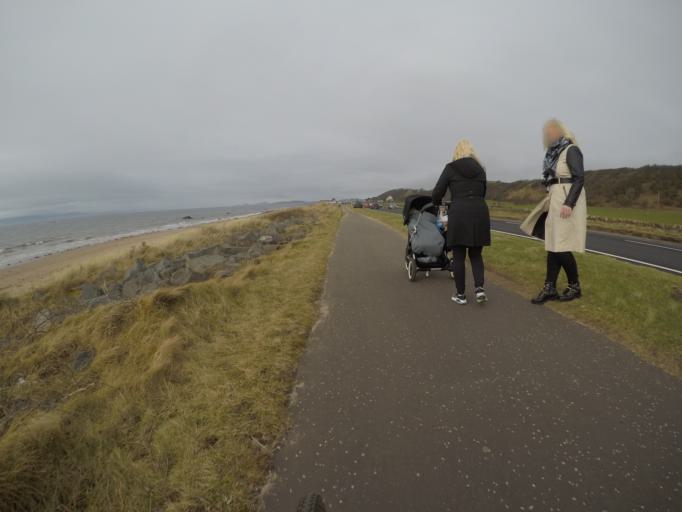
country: GB
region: Scotland
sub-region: North Ayrshire
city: West Kilbride
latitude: 55.6628
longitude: -4.8339
